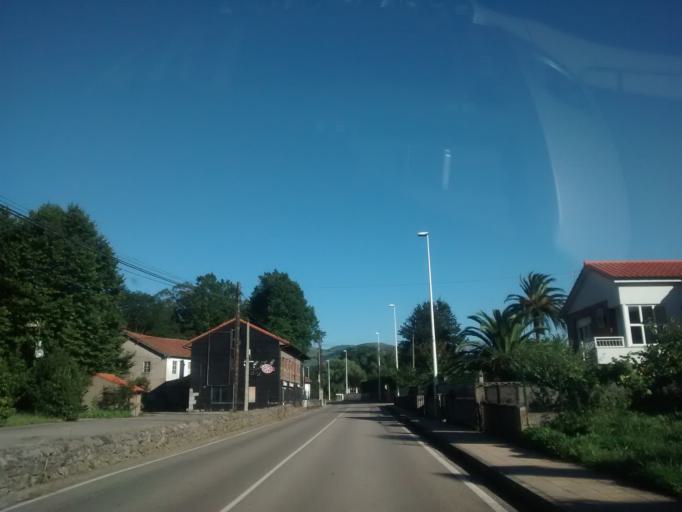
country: ES
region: Cantabria
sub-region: Provincia de Cantabria
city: Entrambasaguas
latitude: 43.3816
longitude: -3.6879
